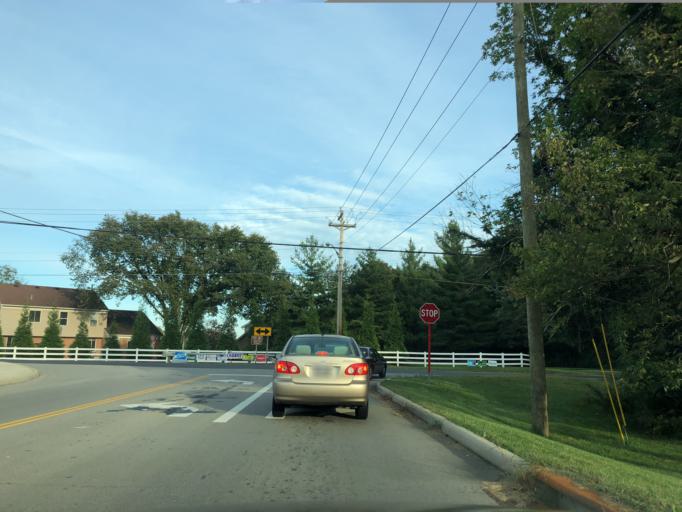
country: US
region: Ohio
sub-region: Hamilton County
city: Loveland
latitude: 39.2809
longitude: -84.2848
